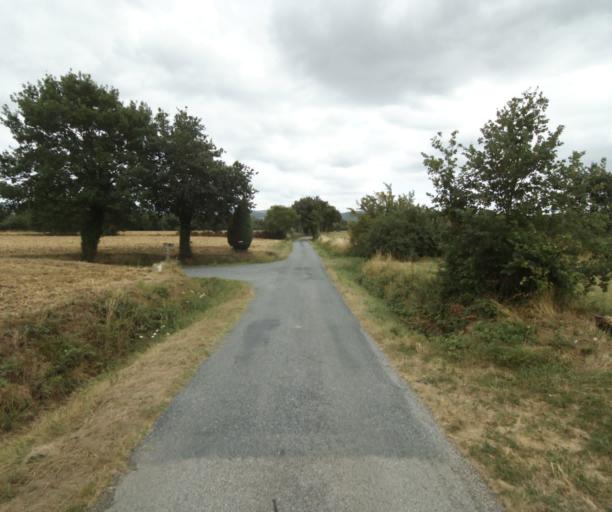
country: FR
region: Midi-Pyrenees
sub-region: Departement du Tarn
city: Soreze
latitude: 43.4827
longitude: 2.0440
